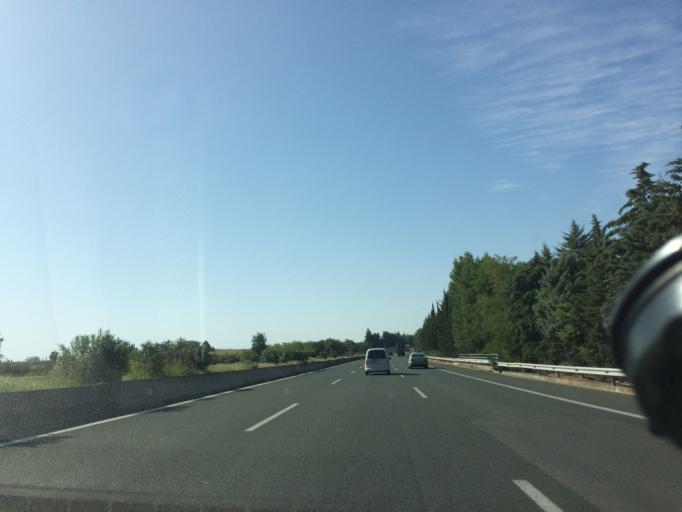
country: GR
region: Central Macedonia
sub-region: Nomos Pierias
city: Kitros
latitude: 40.3732
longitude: 22.6063
